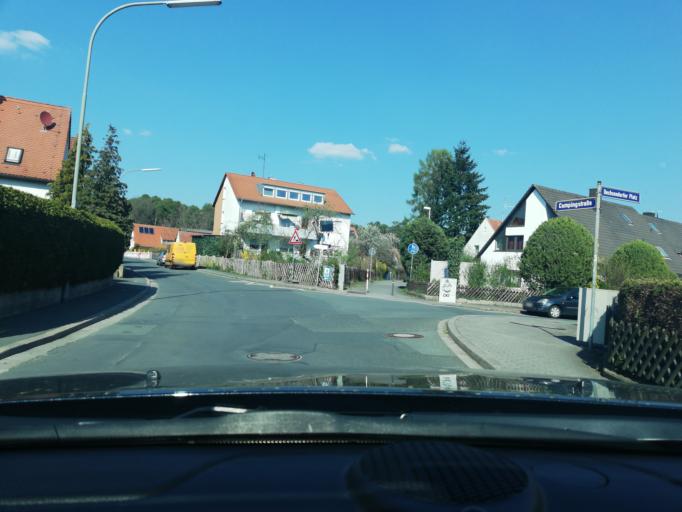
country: DE
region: Bavaria
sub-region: Regierungsbezirk Mittelfranken
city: Hessdorf
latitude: 49.6297
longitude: 10.9413
